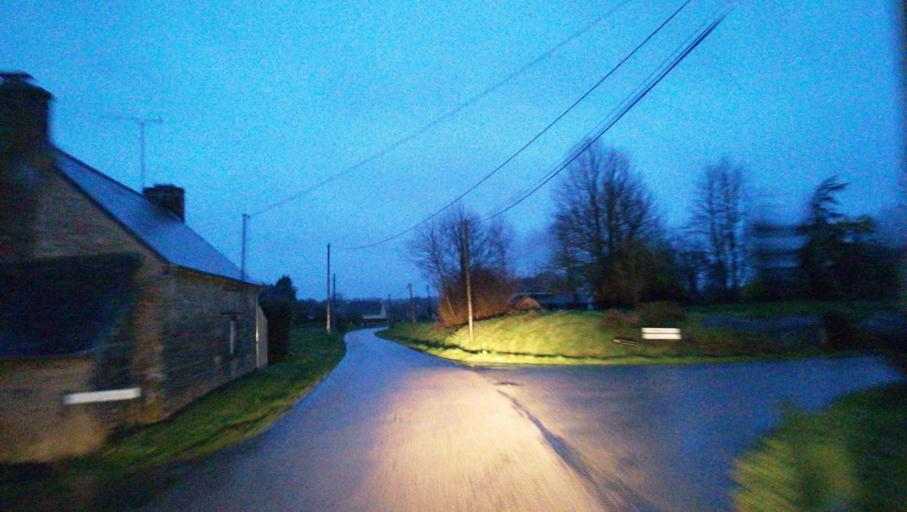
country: FR
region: Brittany
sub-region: Departement des Cotes-d'Armor
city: Plouagat
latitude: 48.4797
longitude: -2.9702
